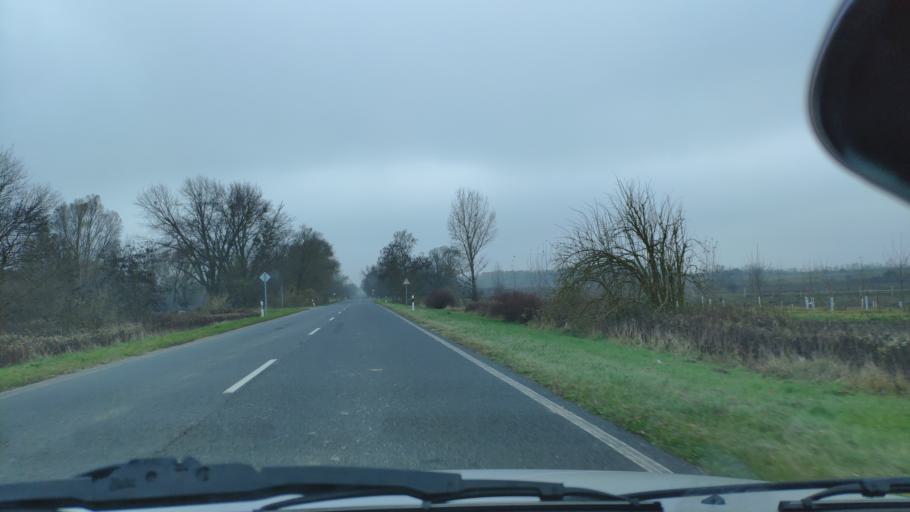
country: HU
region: Somogy
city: Balatonbereny
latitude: 46.6127
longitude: 17.2765
